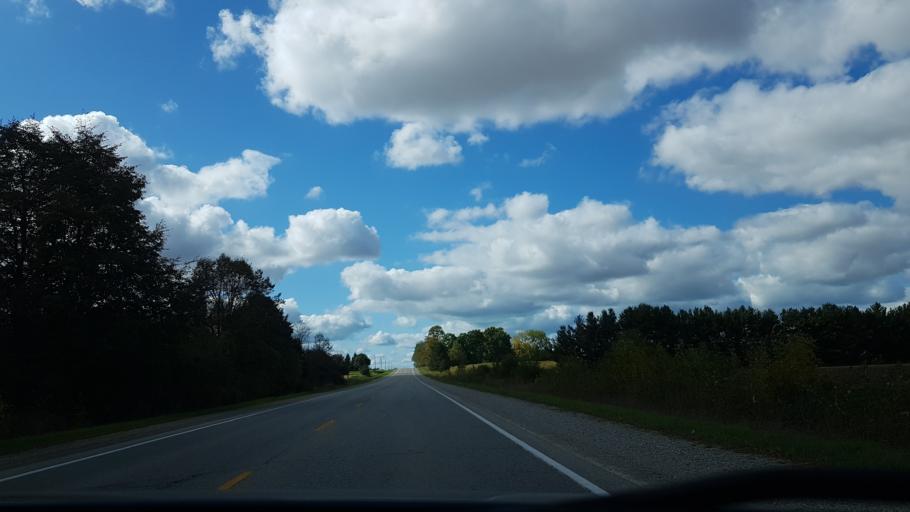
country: CA
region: Ontario
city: South Huron
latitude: 43.3527
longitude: -81.5698
